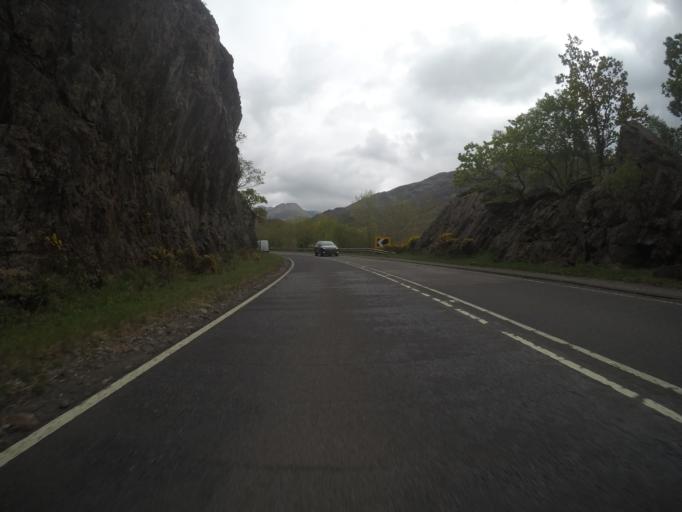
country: GB
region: Scotland
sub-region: Highland
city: Fort William
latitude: 57.2157
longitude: -5.4235
